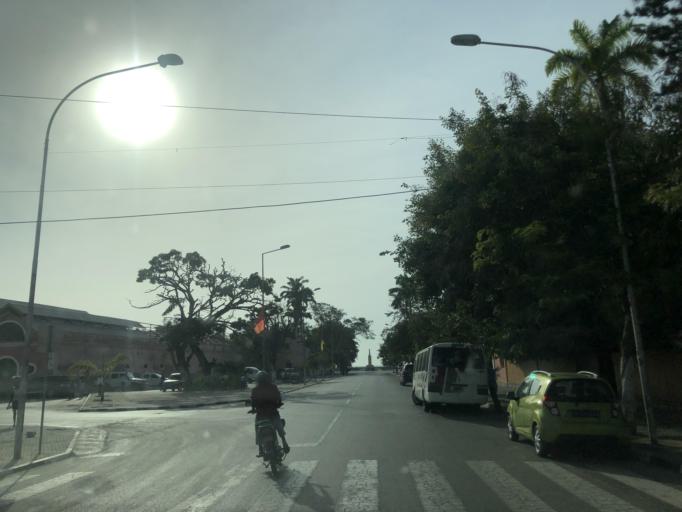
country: AO
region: Benguela
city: Benguela
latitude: -12.5777
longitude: 13.3980
